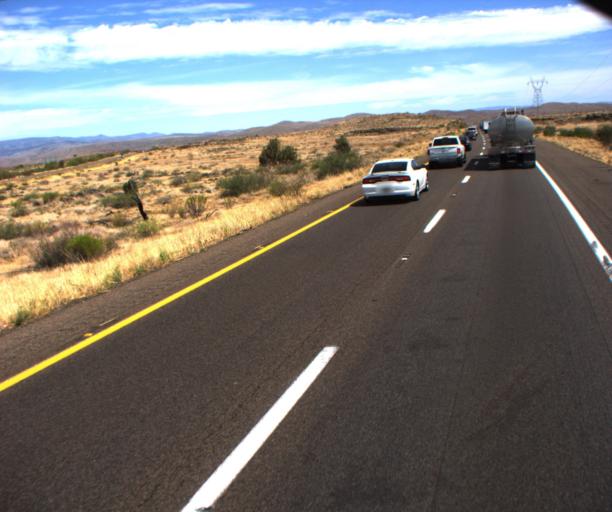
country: US
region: Arizona
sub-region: Yavapai County
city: Cordes Lakes
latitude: 34.2204
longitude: -112.1106
